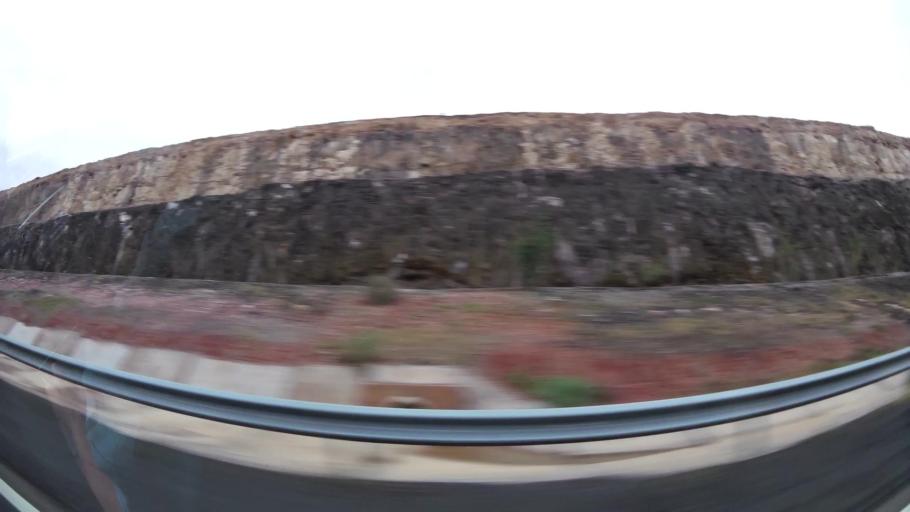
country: MA
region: Taza-Al Hoceima-Taounate
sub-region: Taza
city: Guercif
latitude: 34.3906
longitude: -3.2174
